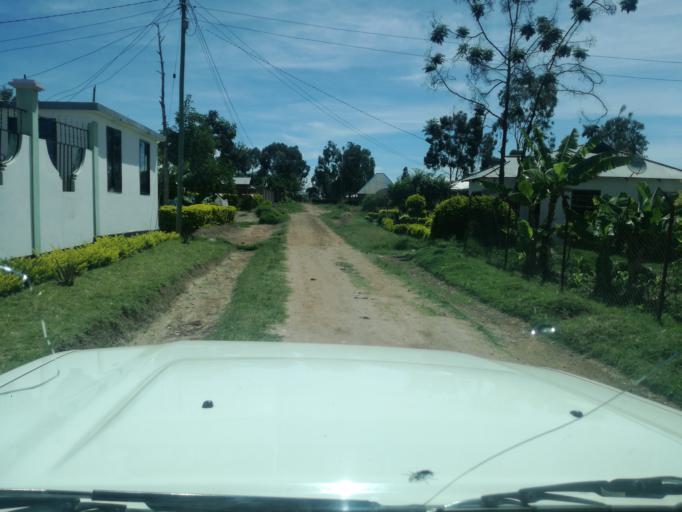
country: TZ
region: Mara
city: Mugumu
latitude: -1.8469
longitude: 34.6620
